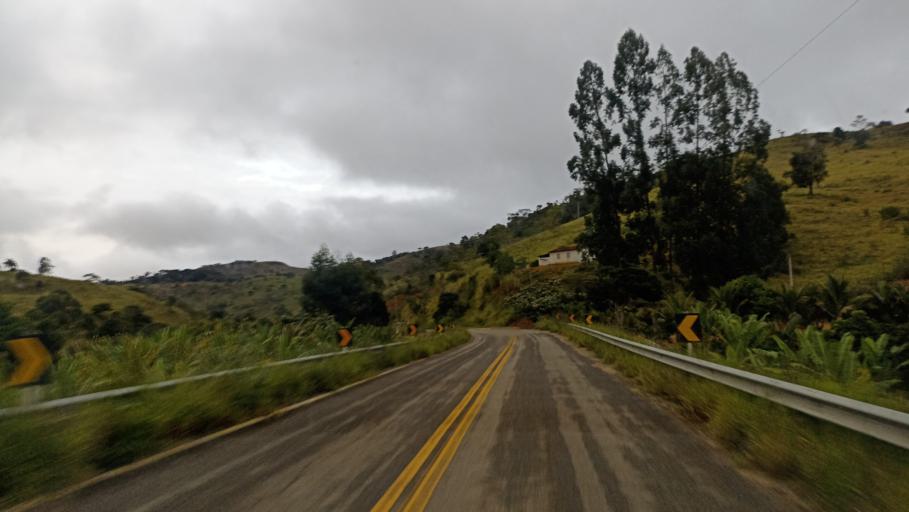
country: BR
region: Bahia
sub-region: Itanhem
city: Itanhem
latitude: -16.6938
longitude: -40.5085
